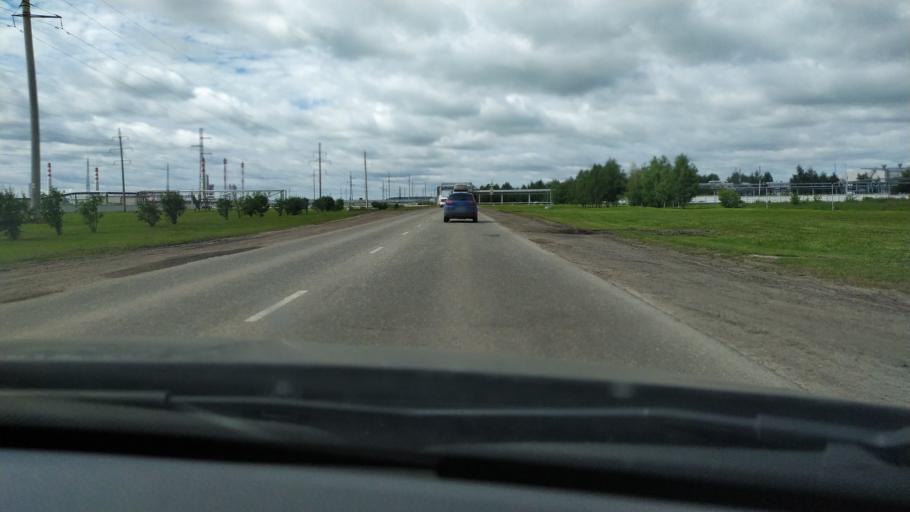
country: RU
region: Perm
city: Kondratovo
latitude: 57.9311
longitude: 56.1240
